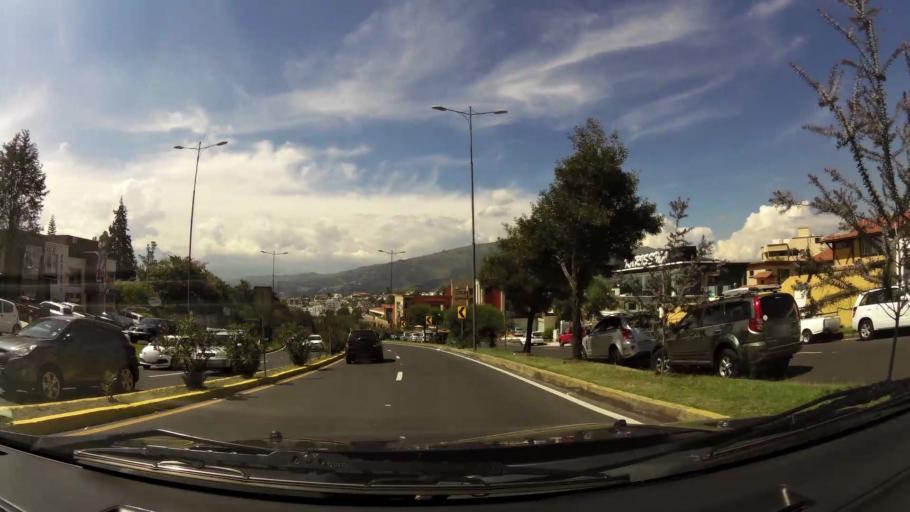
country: EC
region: Pichincha
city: Quito
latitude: -0.2035
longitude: -78.4380
